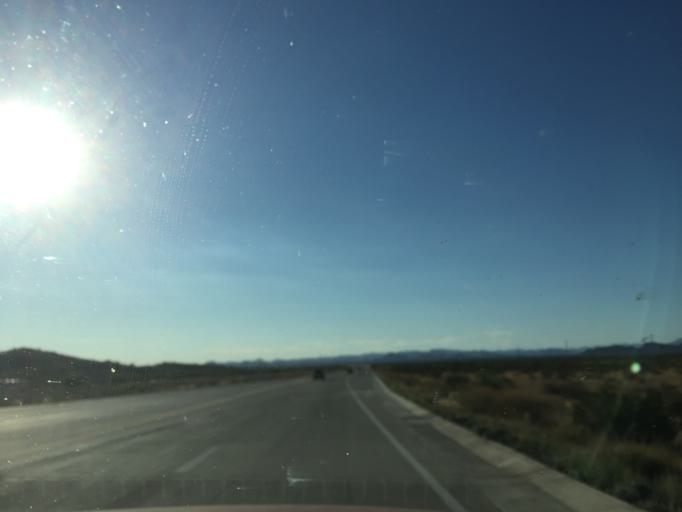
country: US
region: Arizona
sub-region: Maricopa County
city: Anthem
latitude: 33.7719
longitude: -112.1742
